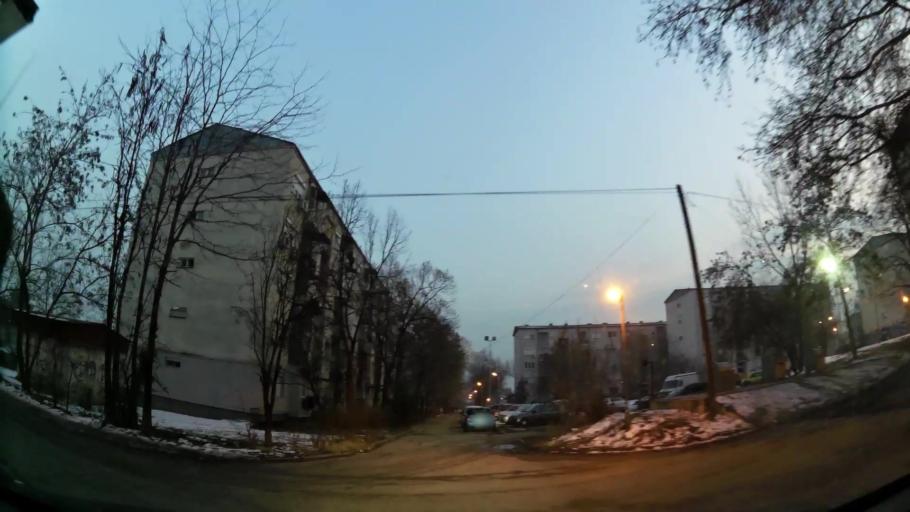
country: MK
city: Creshevo
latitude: 42.0107
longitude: 21.5101
